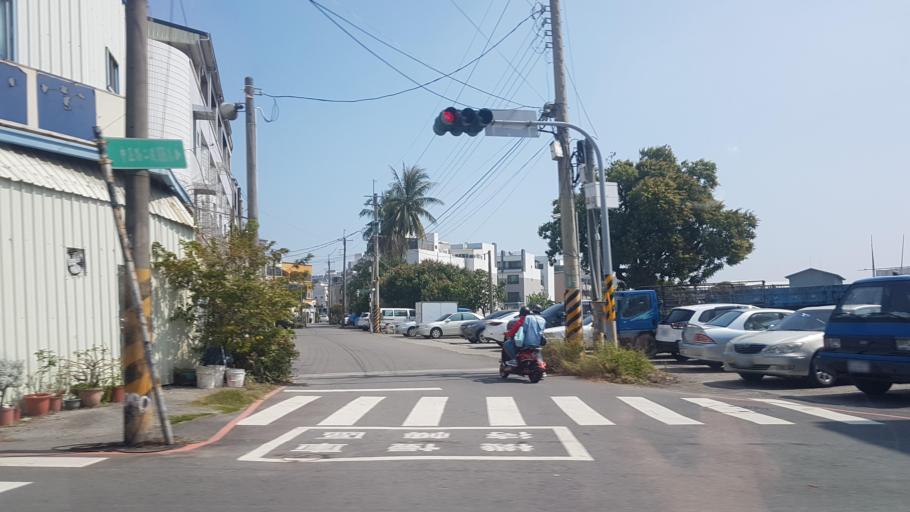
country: TW
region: Taiwan
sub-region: Tainan
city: Tainan
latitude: 22.9459
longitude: 120.2509
